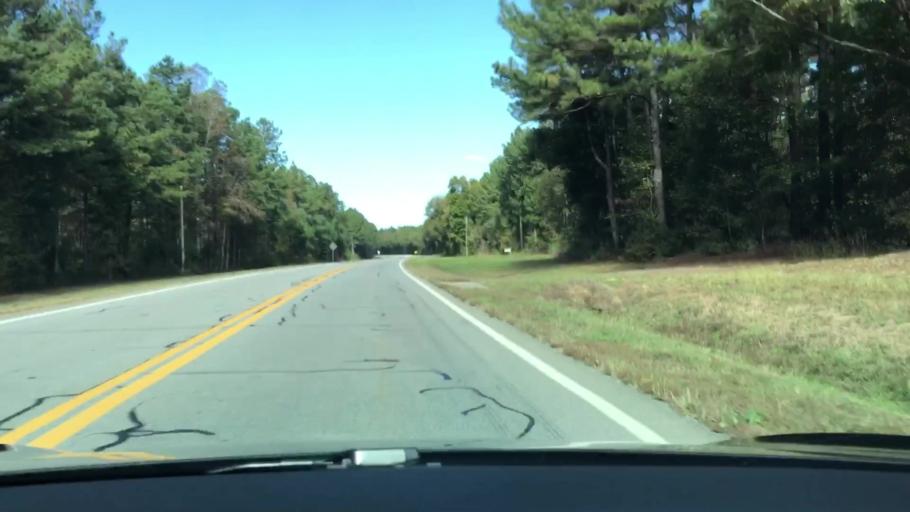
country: US
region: Georgia
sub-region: Warren County
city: Warrenton
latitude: 33.3488
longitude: -82.5840
